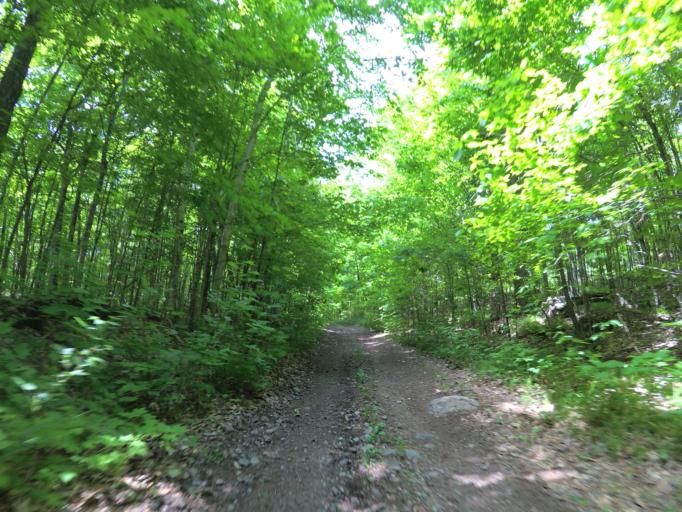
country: CA
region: Ontario
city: Renfrew
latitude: 45.0572
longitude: -76.8641
